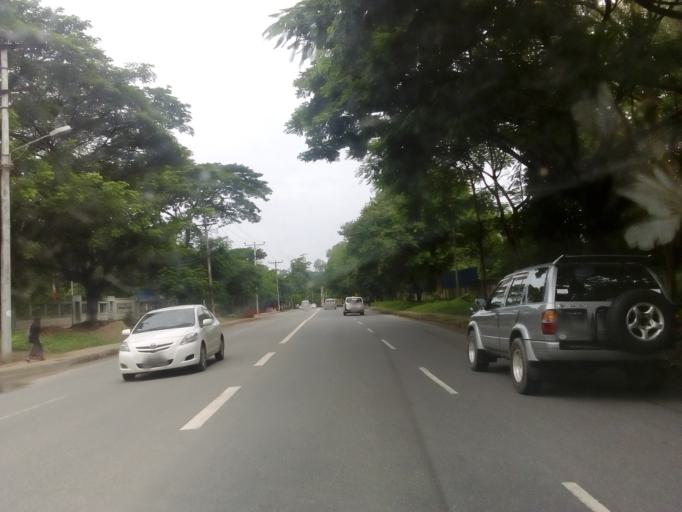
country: MM
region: Yangon
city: Yangon
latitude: 16.8564
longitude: 96.1324
